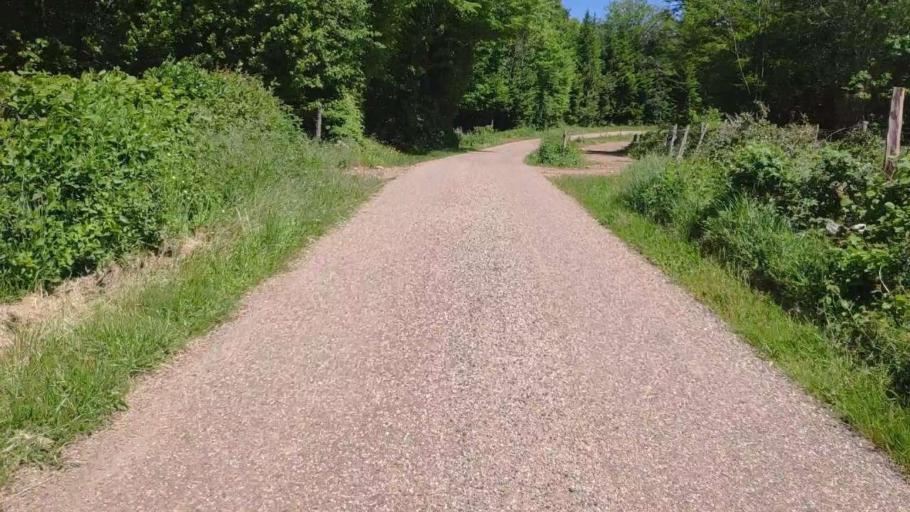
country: FR
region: Franche-Comte
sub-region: Departement du Jura
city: Perrigny
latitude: 46.7250
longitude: 5.6613
